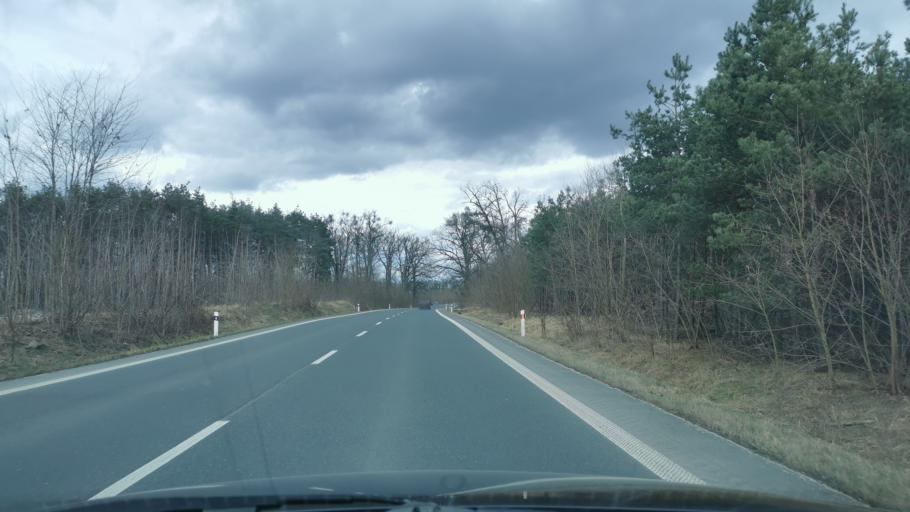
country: CZ
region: South Moravian
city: Tynec
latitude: 48.7412
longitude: 17.0602
